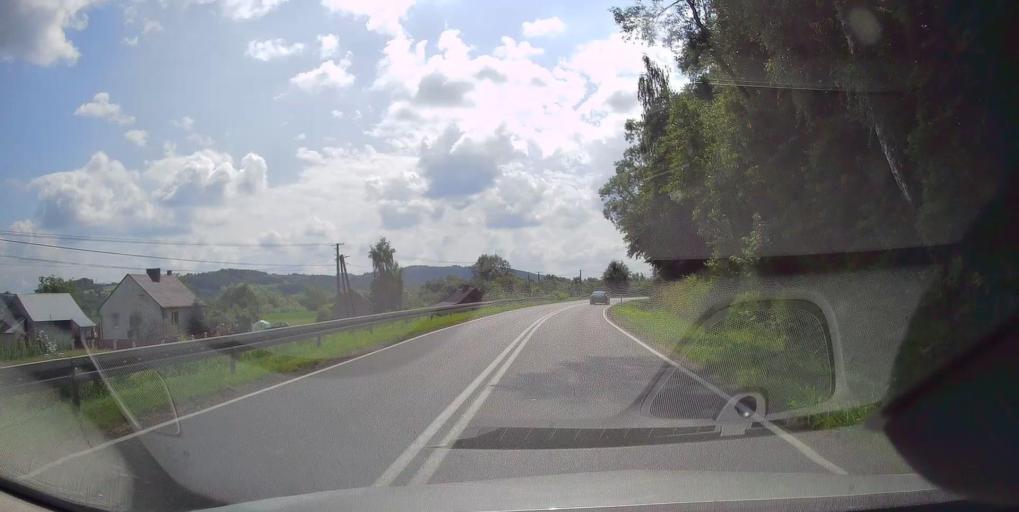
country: PL
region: Lesser Poland Voivodeship
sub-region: Powiat tarnowski
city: Janowice
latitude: 49.8866
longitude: 20.8291
